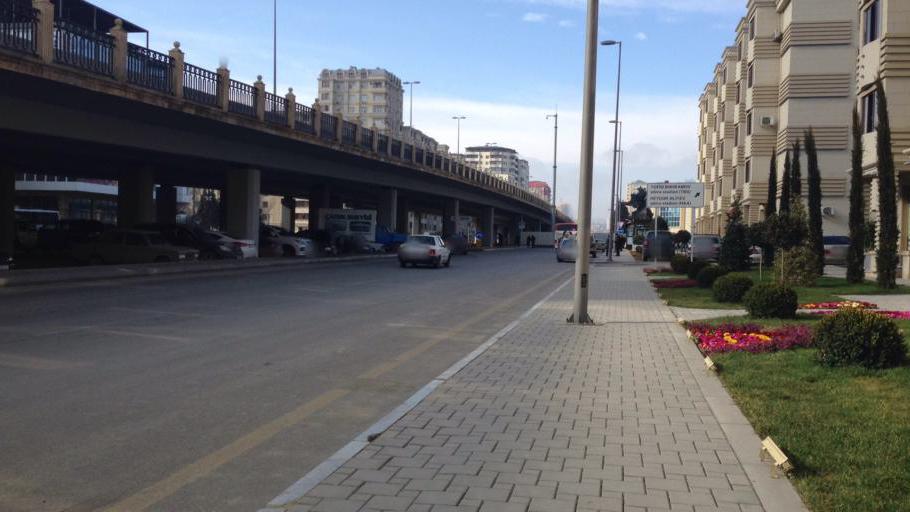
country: AZ
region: Baki
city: Bilajari
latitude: 40.4138
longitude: 49.8481
